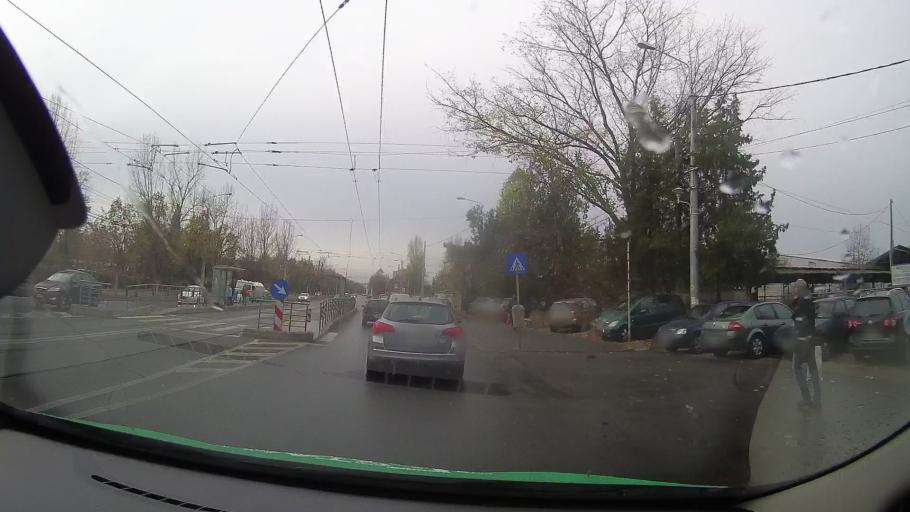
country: RO
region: Prahova
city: Ploiesti
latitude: 44.9427
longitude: 25.9921
